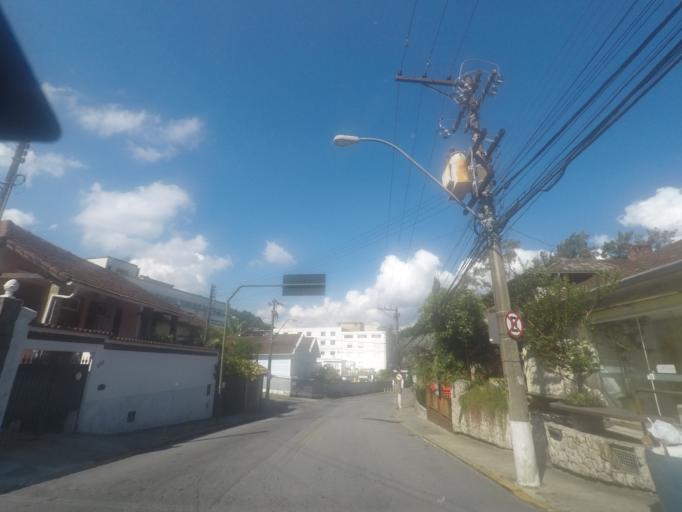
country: BR
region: Rio de Janeiro
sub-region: Petropolis
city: Petropolis
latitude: -22.5197
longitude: -43.1942
